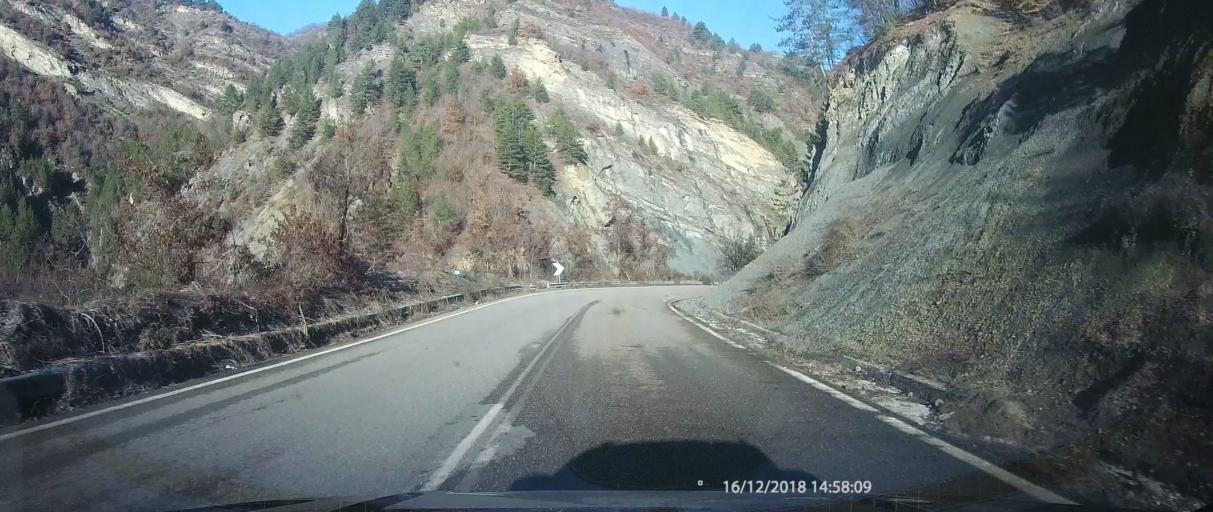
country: GR
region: West Macedonia
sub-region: Nomos Kastorias
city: Nestorio
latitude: 40.2216
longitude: 21.0295
